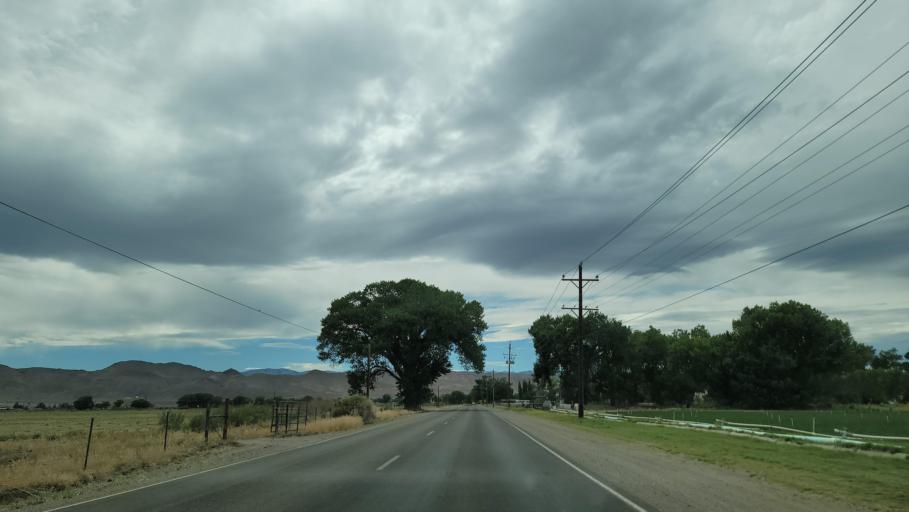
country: US
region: Nevada
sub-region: Lyon County
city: Yerington
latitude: 39.0481
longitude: -119.1749
